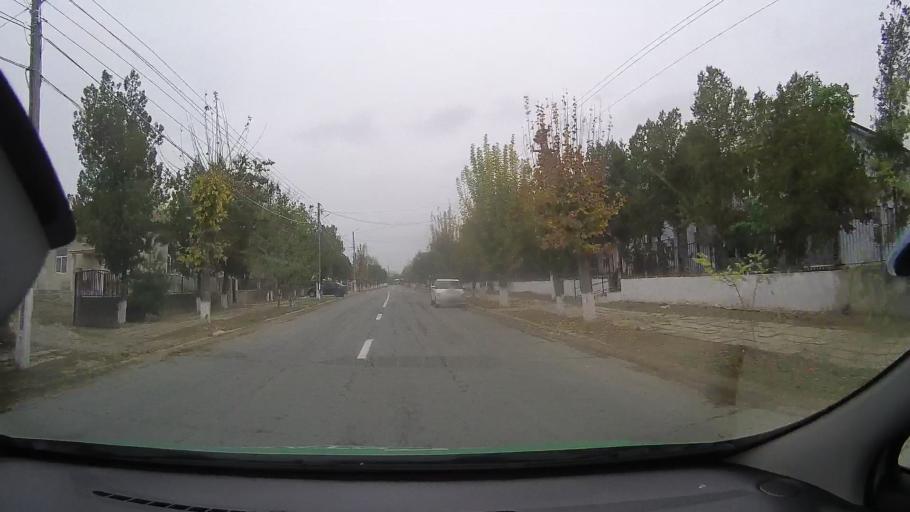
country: RO
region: Constanta
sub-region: Comuna Pantelimon
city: Pantelimon
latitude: 44.5448
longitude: 28.3290
